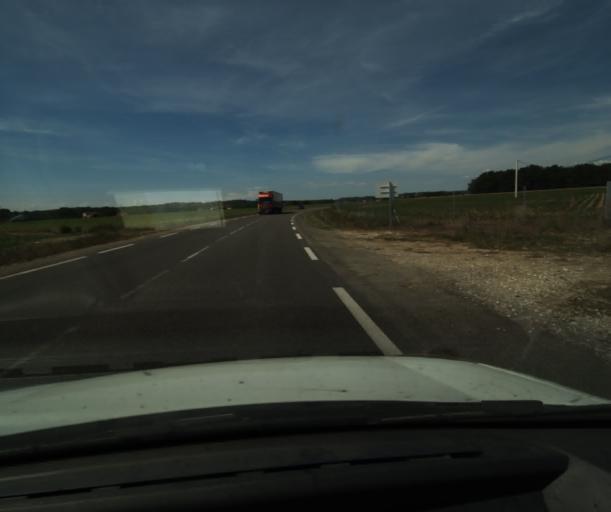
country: FR
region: Midi-Pyrenees
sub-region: Departement du Tarn-et-Garonne
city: Moissac
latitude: 44.0775
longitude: 1.1139
